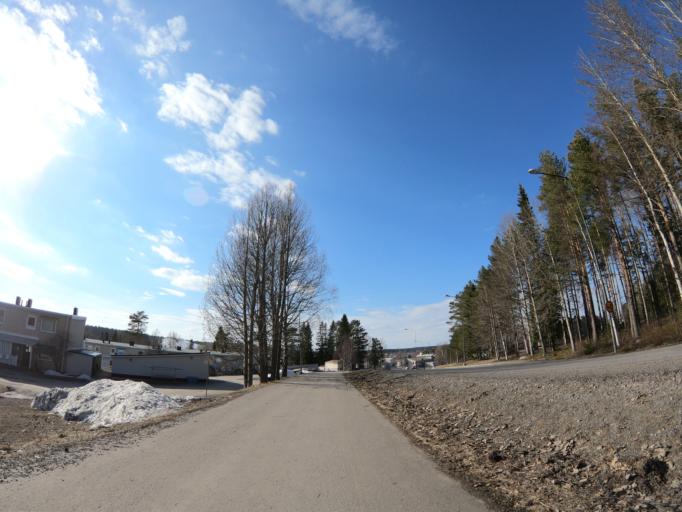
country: SE
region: Vaesterbotten
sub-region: Umea Kommun
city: Ersmark
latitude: 63.8383
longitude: 20.3243
